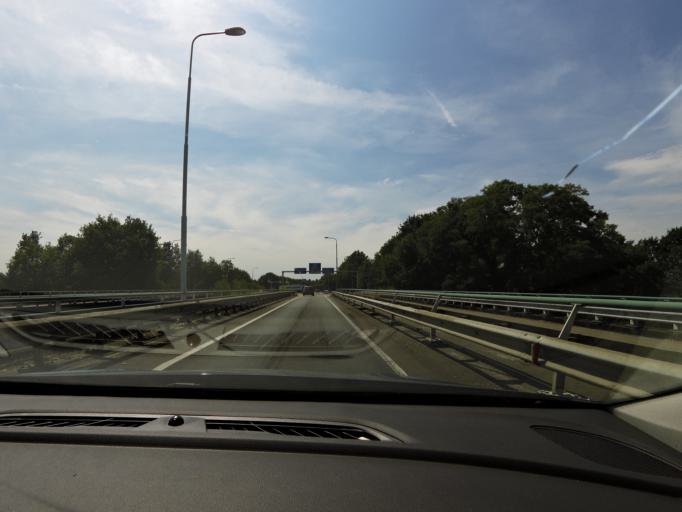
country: NL
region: Limburg
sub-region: Gemeente Leudal
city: Kelpen-Oler
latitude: 51.1804
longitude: 5.8492
